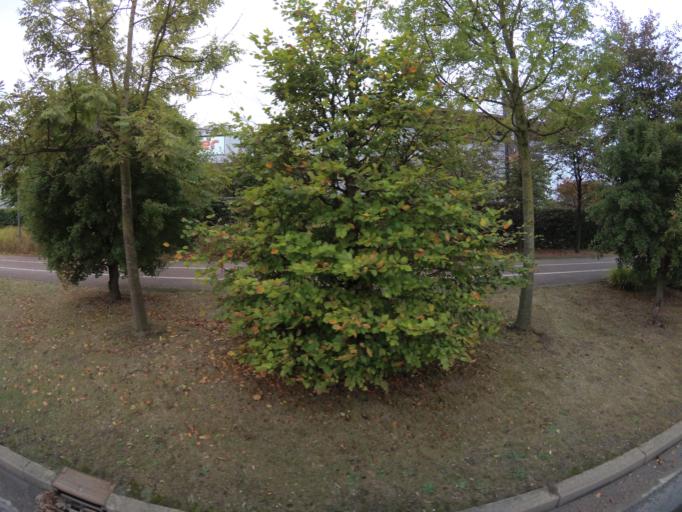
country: FR
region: Ile-de-France
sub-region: Departement de Seine-et-Marne
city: Chanteloup-en-Brie
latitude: 48.8558
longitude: 2.7561
